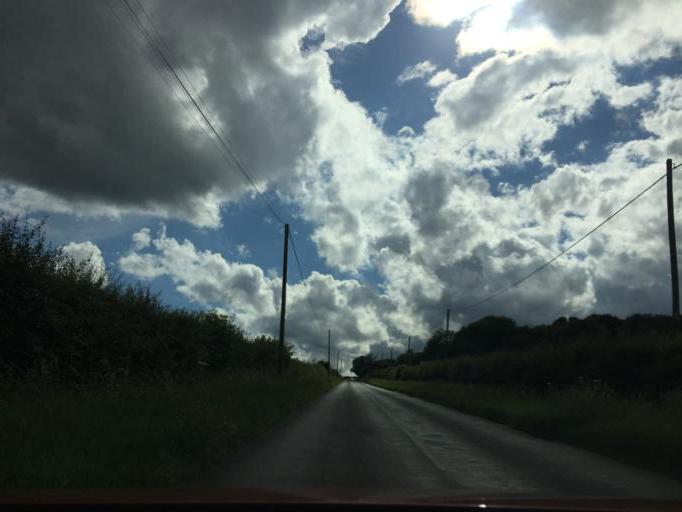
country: GB
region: England
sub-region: Hertfordshire
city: Harpenden
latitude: 51.8486
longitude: -0.3784
